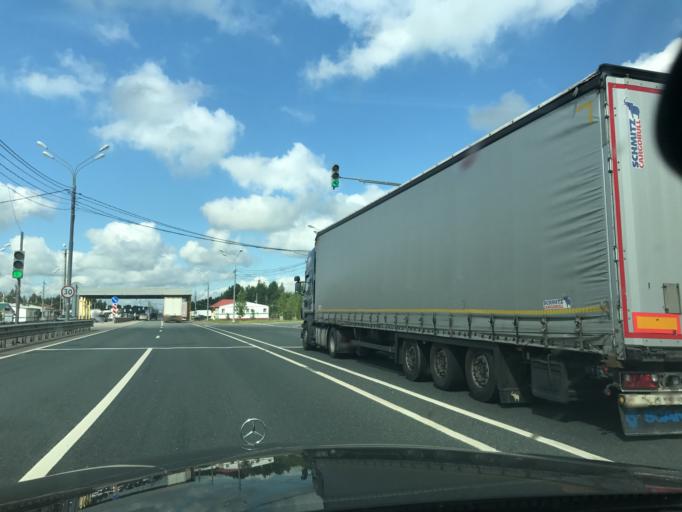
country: RU
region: Smolensk
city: Rudnya
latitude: 54.6912
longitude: 31.0192
